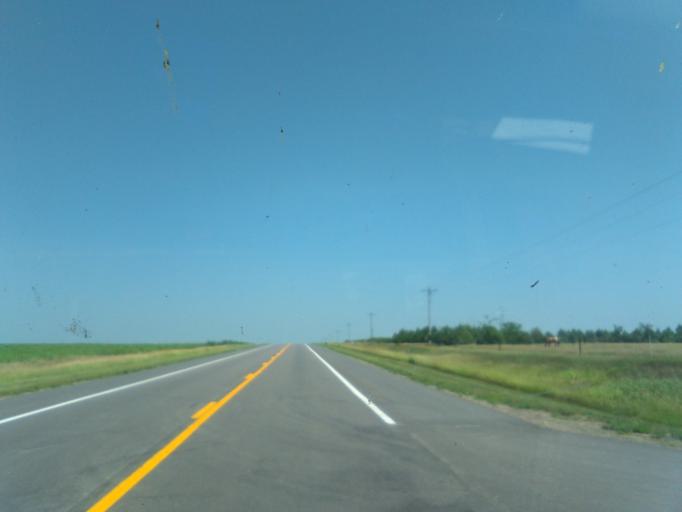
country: US
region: Nebraska
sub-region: Red Willow County
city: McCook
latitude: 40.3035
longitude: -100.6495
